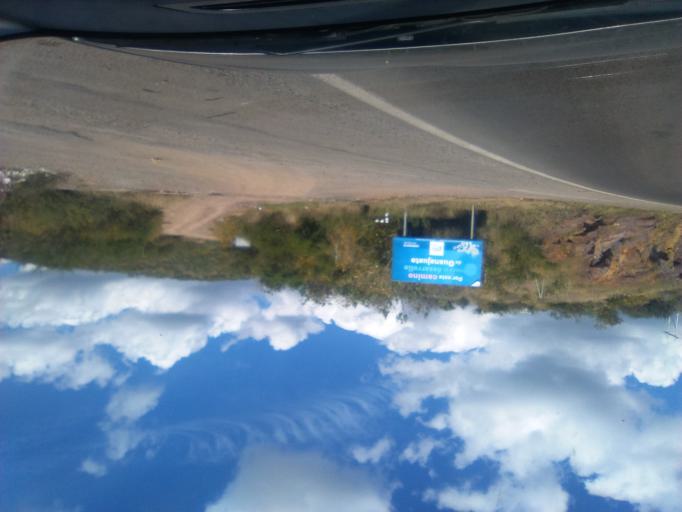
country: MX
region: Guanajuato
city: Marfil
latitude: 21.0009
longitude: -101.2706
